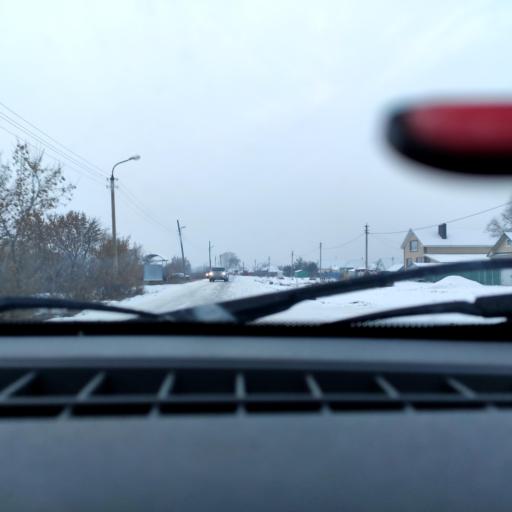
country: RU
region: Bashkortostan
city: Blagoveshchensk
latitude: 54.8963
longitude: 56.0244
